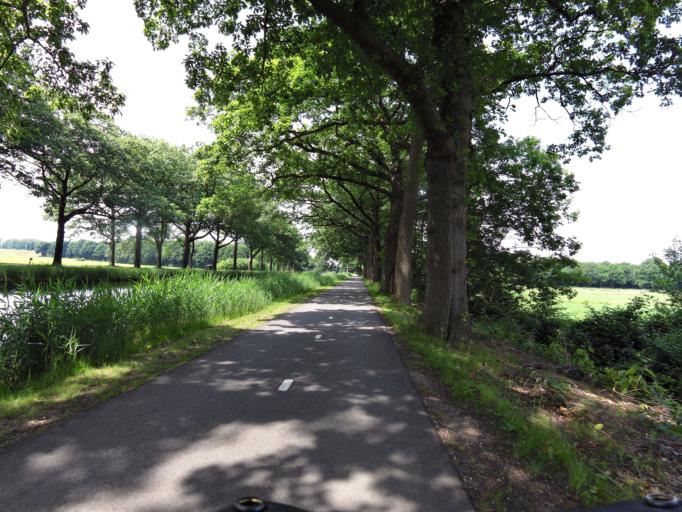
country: NL
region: Gelderland
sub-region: Gemeente Apeldoorn
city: Loenen
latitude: 52.1564
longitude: 6.0212
